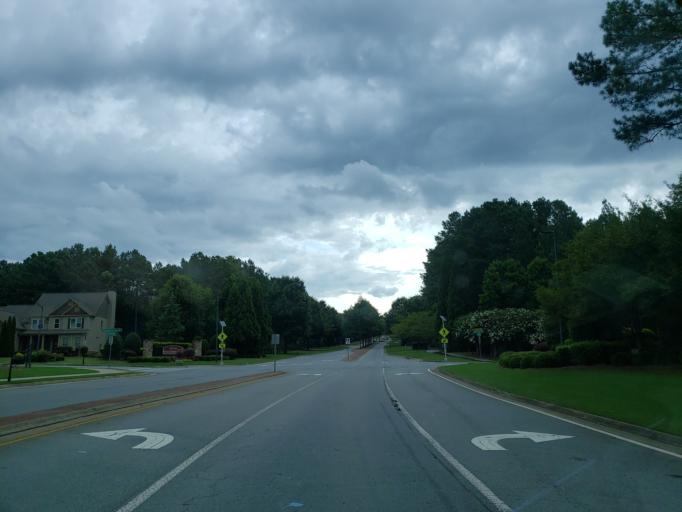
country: US
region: Georgia
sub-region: Bartow County
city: Emerson
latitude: 34.0251
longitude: -84.7827
